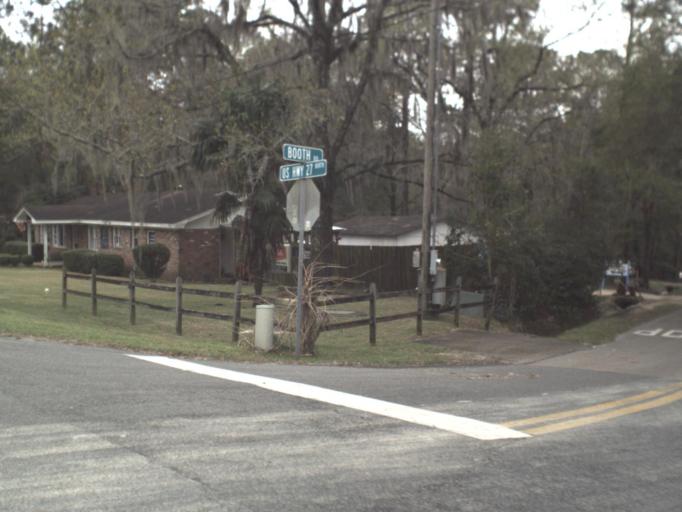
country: US
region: Florida
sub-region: Leon County
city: Tallahassee
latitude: 30.5071
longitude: -84.3341
